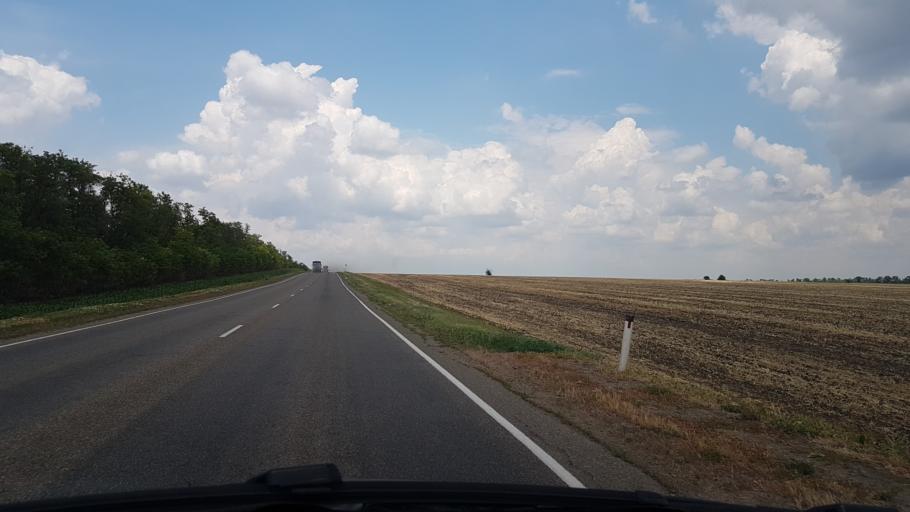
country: RU
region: Krasnodarskiy
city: Dmitriyevskaya
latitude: 45.6756
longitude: 40.7441
